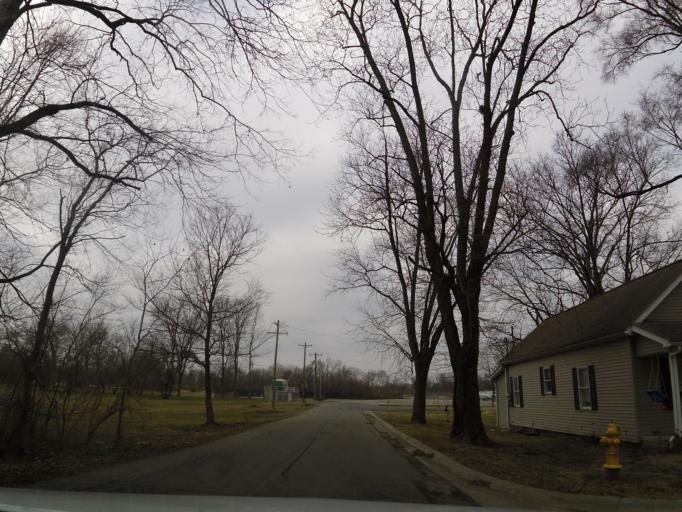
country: US
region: Indiana
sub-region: Bartholomew County
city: Columbus
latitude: 39.1976
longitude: -85.9084
